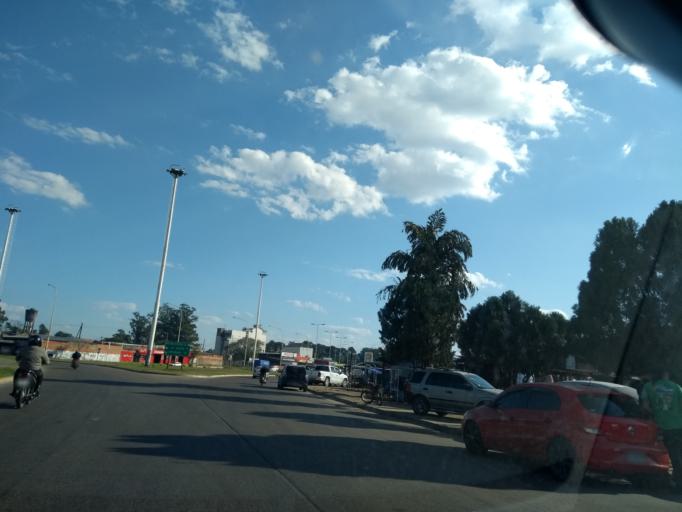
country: AR
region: Corrientes
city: Corrientes
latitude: -27.4840
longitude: -58.7819
